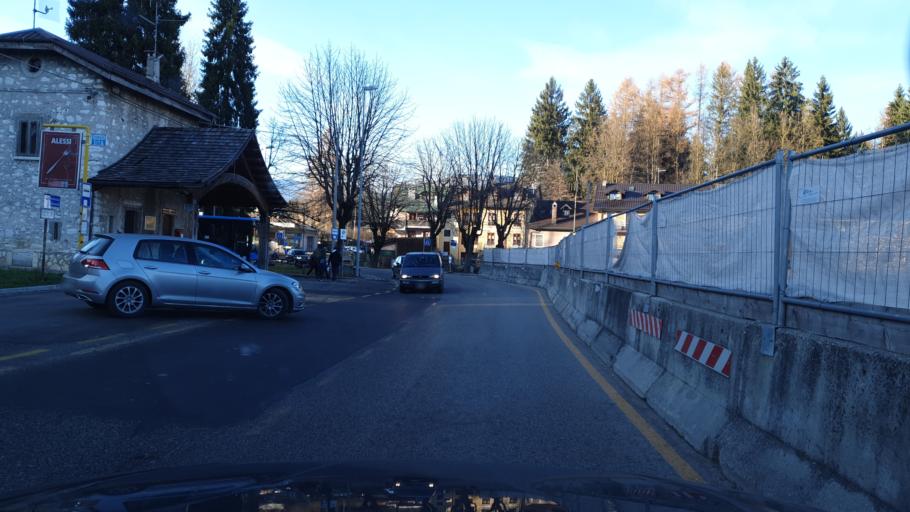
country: IT
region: Veneto
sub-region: Provincia di Vicenza
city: Asiago
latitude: 45.8729
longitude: 11.5067
